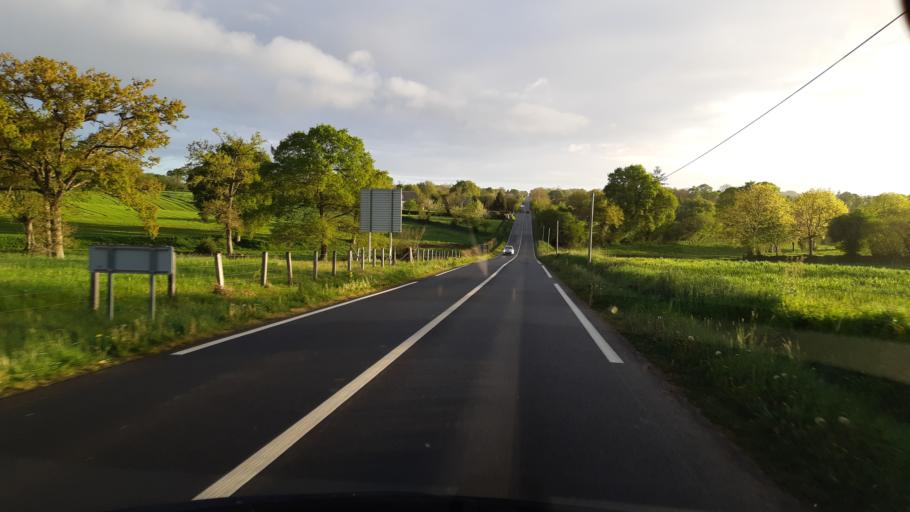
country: FR
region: Lower Normandy
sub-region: Departement de la Manche
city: Percy
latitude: 48.9991
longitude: -1.1540
